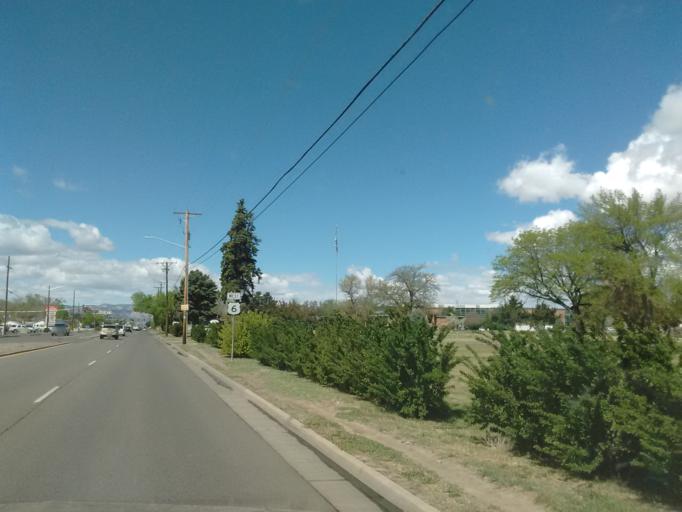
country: US
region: Colorado
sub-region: Mesa County
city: Fruitvale
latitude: 39.0774
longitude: -108.5015
